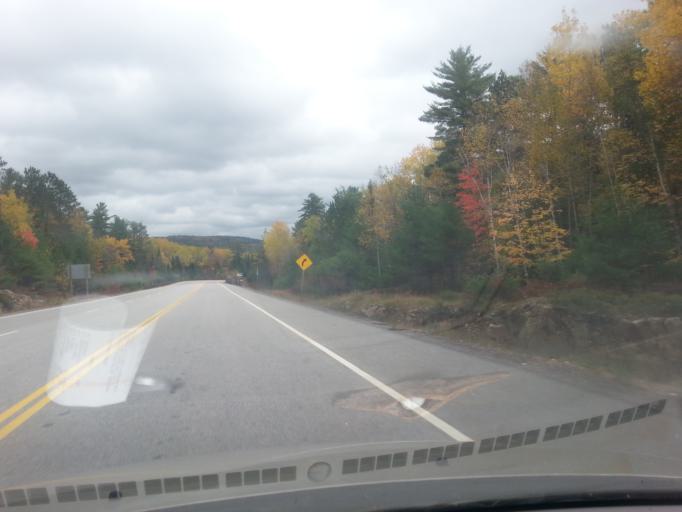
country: CA
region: Ontario
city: Mattawa
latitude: 46.2835
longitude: -78.4012
